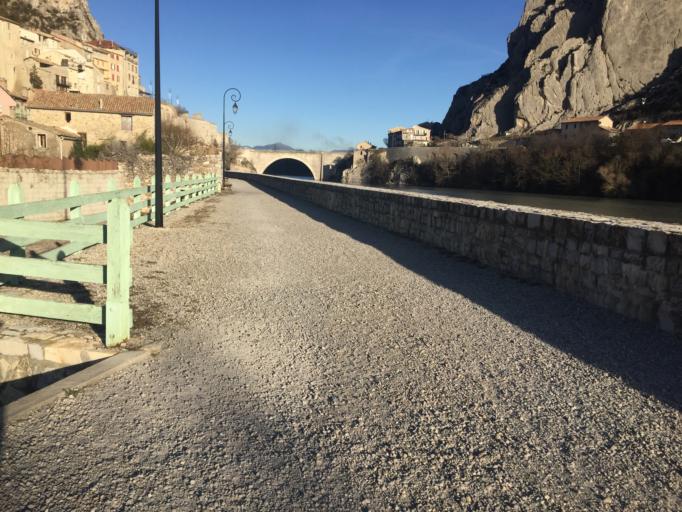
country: FR
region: Provence-Alpes-Cote d'Azur
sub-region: Departement des Alpes-de-Haute-Provence
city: Sisteron
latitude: 44.1969
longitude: 5.9467
